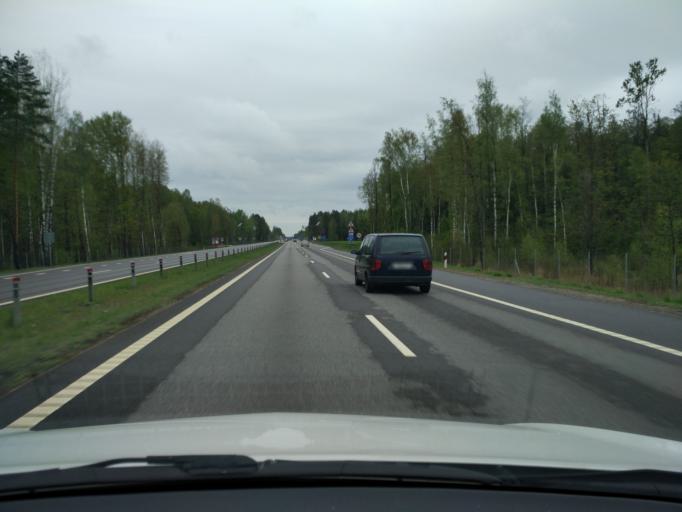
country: BY
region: Mogilev
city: Asipovichy
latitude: 53.3817
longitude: 28.5598
